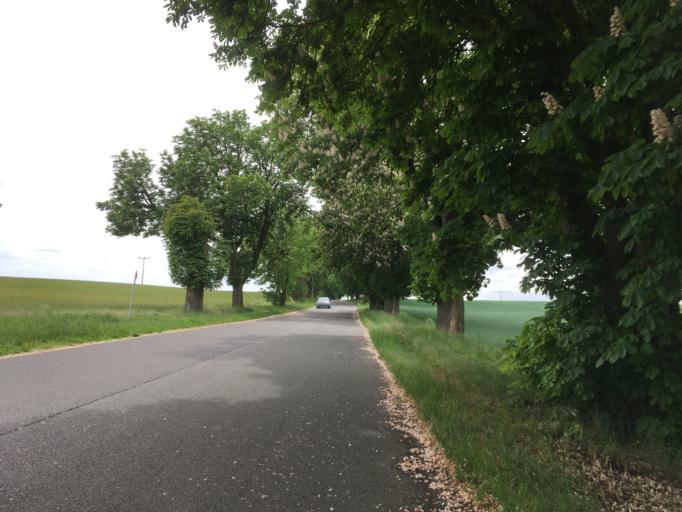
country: DE
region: Brandenburg
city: Melchow
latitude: 52.7263
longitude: 13.7466
